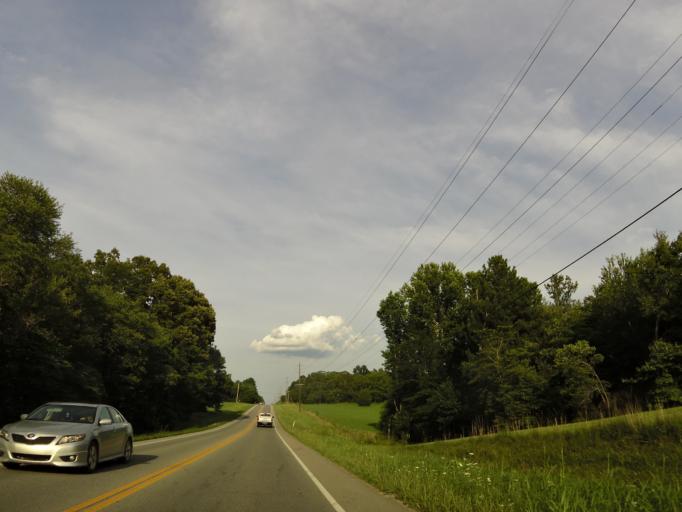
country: US
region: Tennessee
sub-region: Humphreys County
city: McEwen
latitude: 36.0909
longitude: -87.5109
